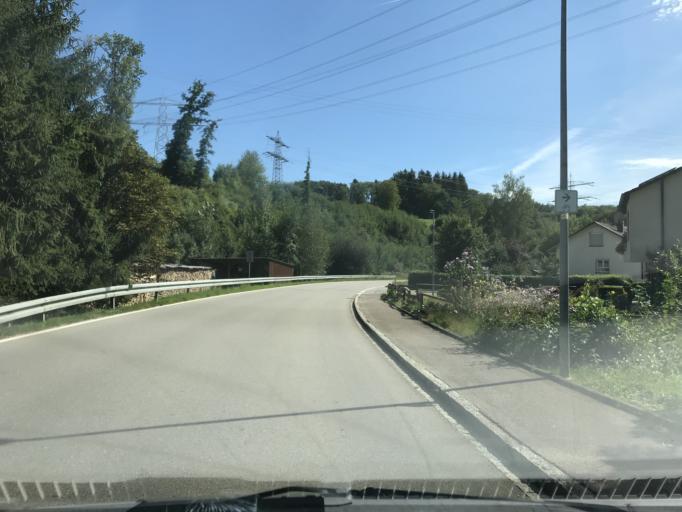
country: DE
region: Baden-Wuerttemberg
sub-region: Freiburg Region
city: Schworstadt
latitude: 47.6037
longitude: 7.8706
